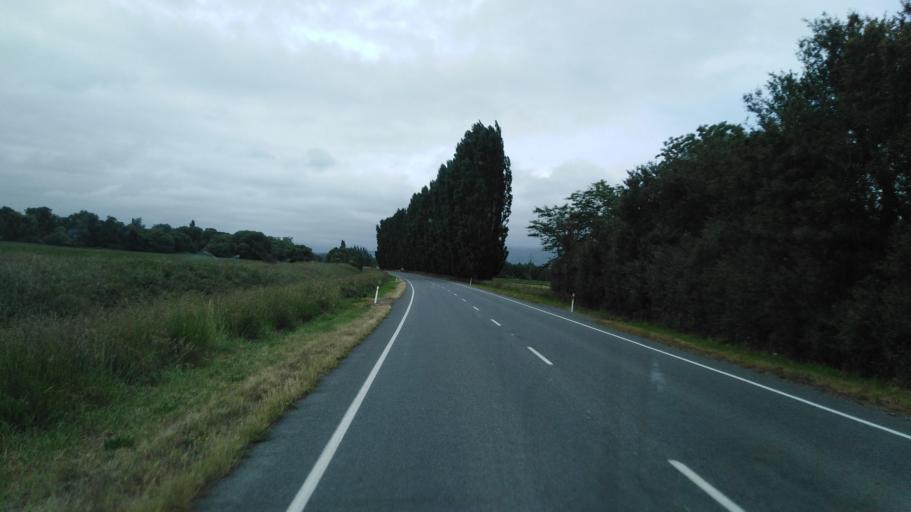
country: NZ
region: Canterbury
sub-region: Kaikoura District
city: Kaikoura
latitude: -42.7339
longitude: 173.2731
